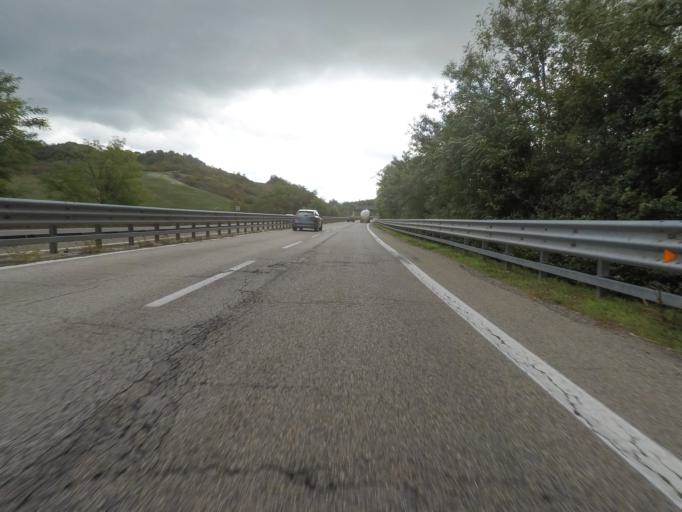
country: IT
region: Tuscany
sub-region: Provincia di Siena
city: Rapolano Terme
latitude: 43.3135
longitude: 11.5783
